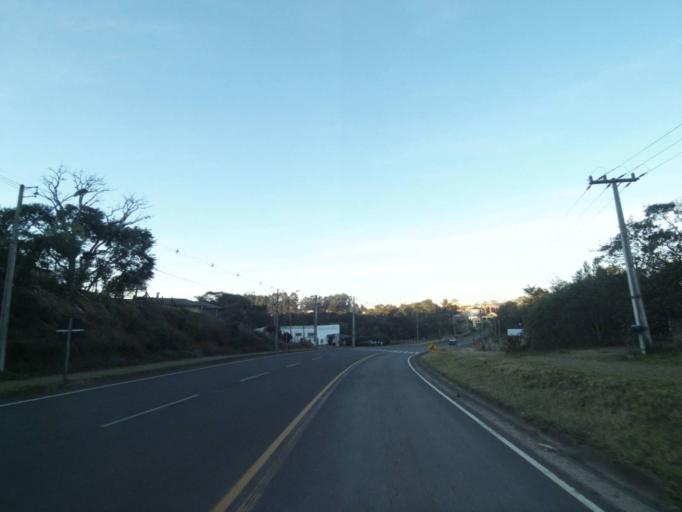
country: BR
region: Parana
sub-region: Tibagi
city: Tibagi
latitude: -24.5122
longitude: -50.4225
